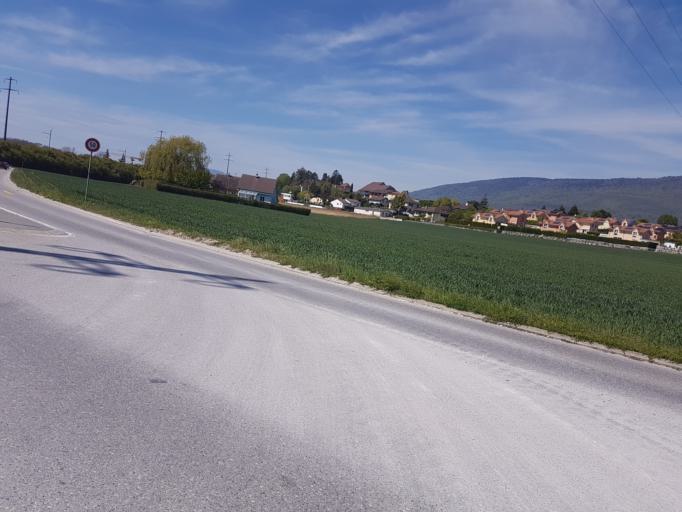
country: CH
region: Neuchatel
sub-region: Neuchatel District
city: Cornaux
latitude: 47.0106
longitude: 7.0248
